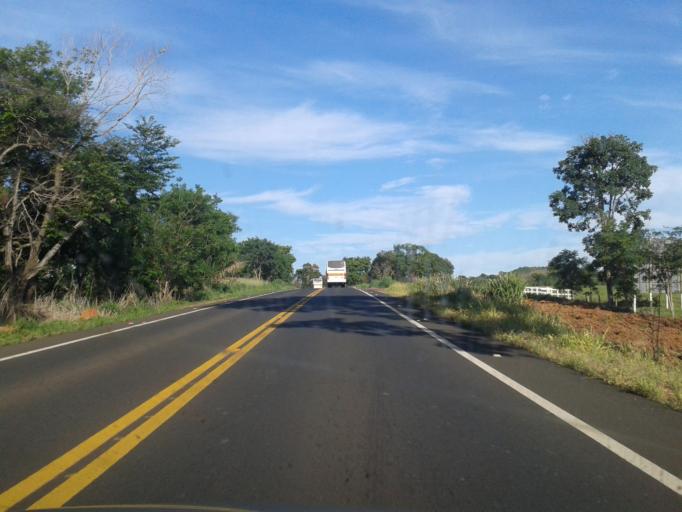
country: BR
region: Goias
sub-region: Caldas Novas
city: Caldas Novas
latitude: -18.1195
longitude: -48.5939
